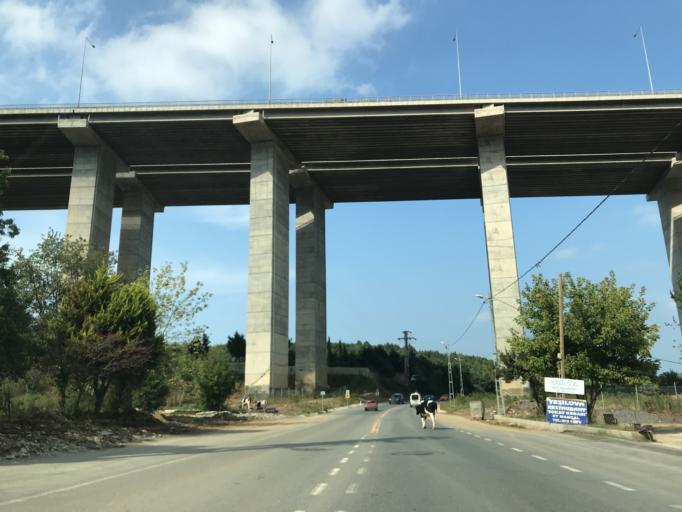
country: TR
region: Istanbul
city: Arikoey
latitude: 41.2248
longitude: 29.0357
